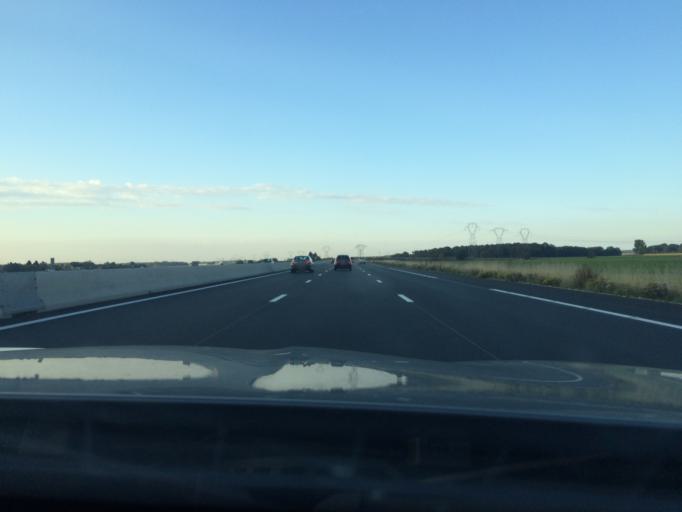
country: FR
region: Ile-de-France
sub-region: Departement de Seine-et-Marne
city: Ponthierry
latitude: 48.5213
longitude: 2.5042
